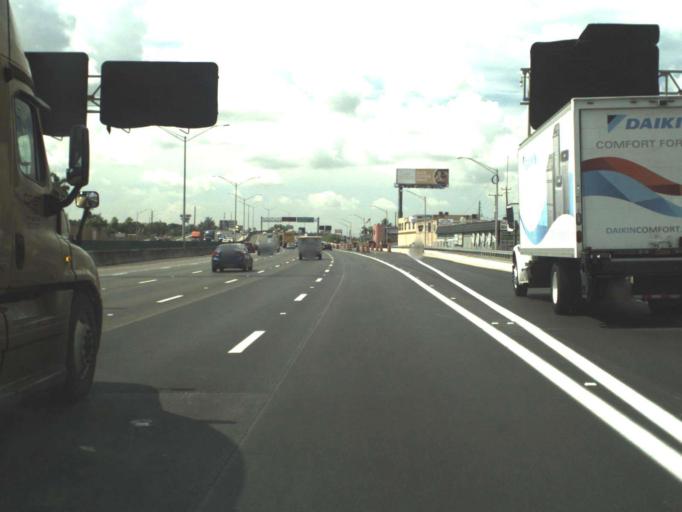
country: US
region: Florida
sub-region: Broward County
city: Pembroke Park
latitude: 26.0025
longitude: -80.1671
